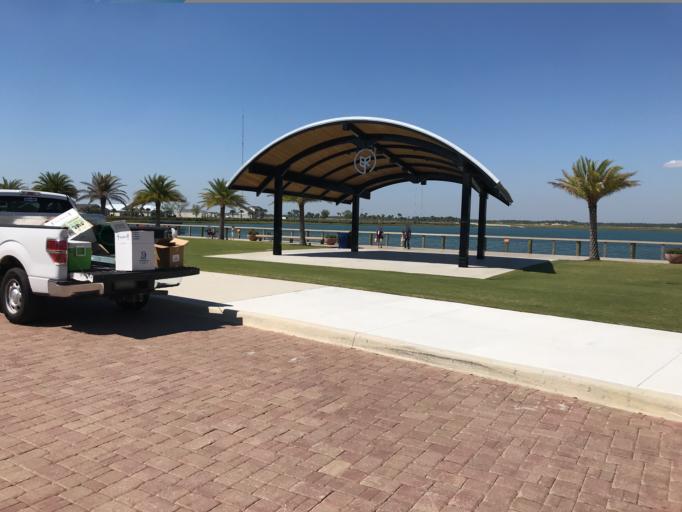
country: US
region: Florida
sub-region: Lee County
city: Olga
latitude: 26.7840
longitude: -81.7466
